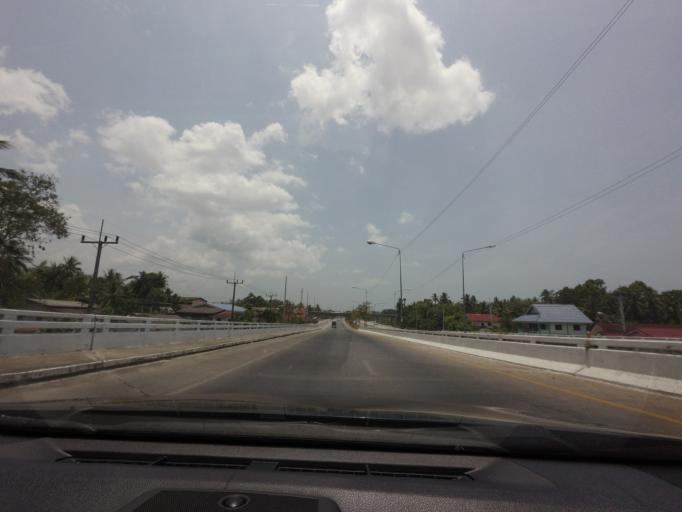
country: TH
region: Pattani
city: Pattani
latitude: 6.8514
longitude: 101.2492
